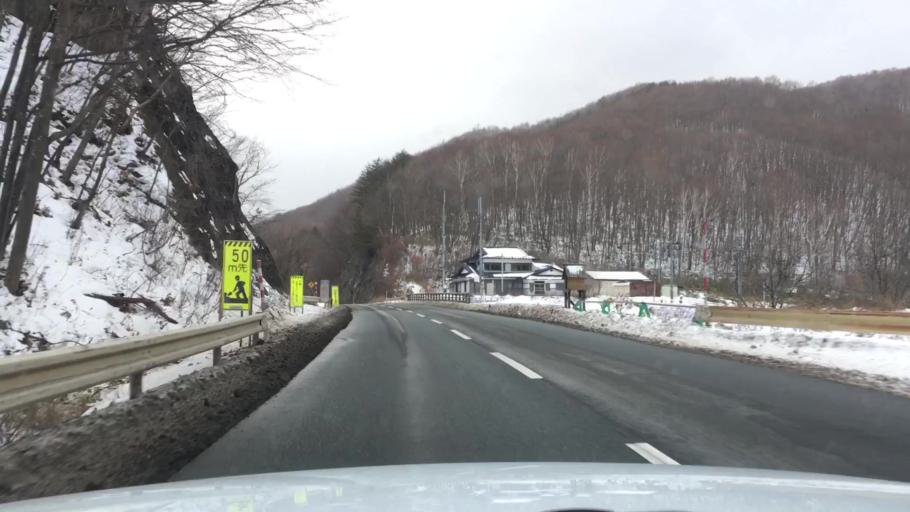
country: JP
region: Iwate
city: Morioka-shi
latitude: 39.6340
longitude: 141.4507
